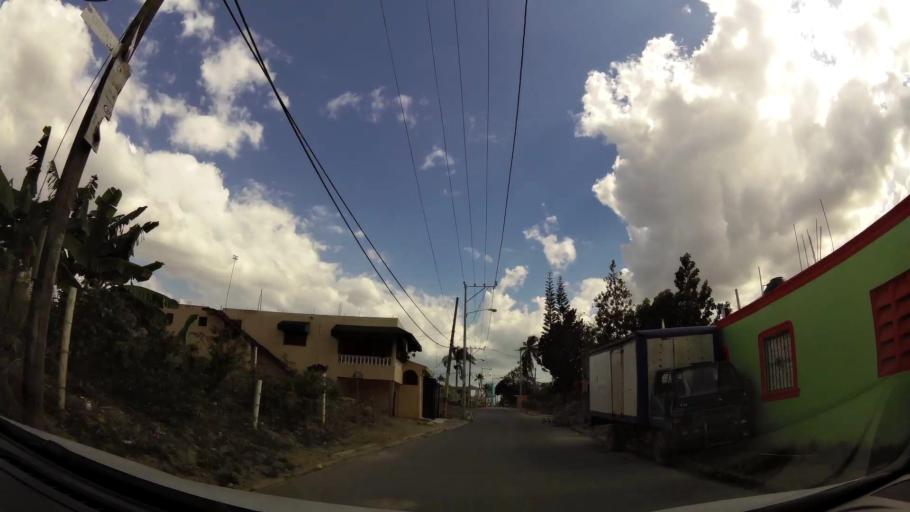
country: DO
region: Nacional
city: Ensanche Luperon
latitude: 18.5330
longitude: -69.8937
